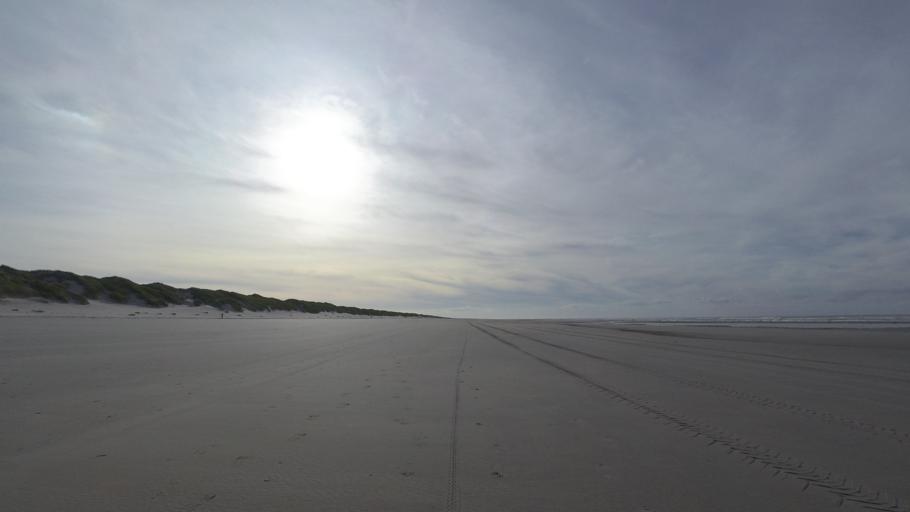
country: NL
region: Friesland
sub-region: Gemeente Ameland
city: Nes
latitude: 53.4652
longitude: 5.8570
